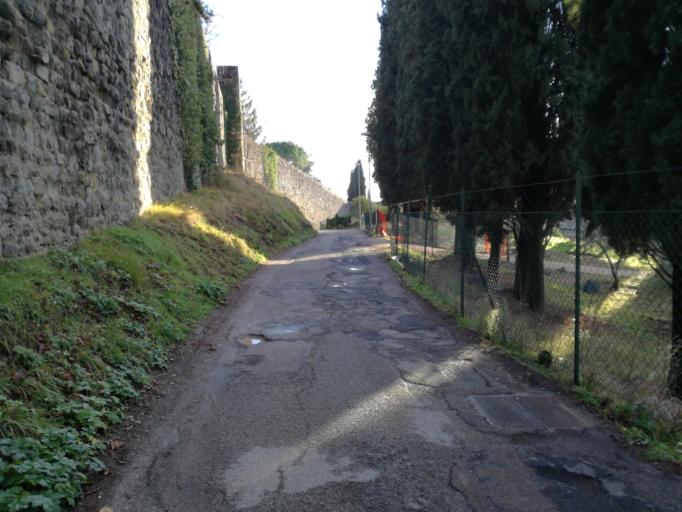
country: IT
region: Umbria
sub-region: Provincia di Perugia
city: Perugia
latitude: 43.1189
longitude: 12.3844
